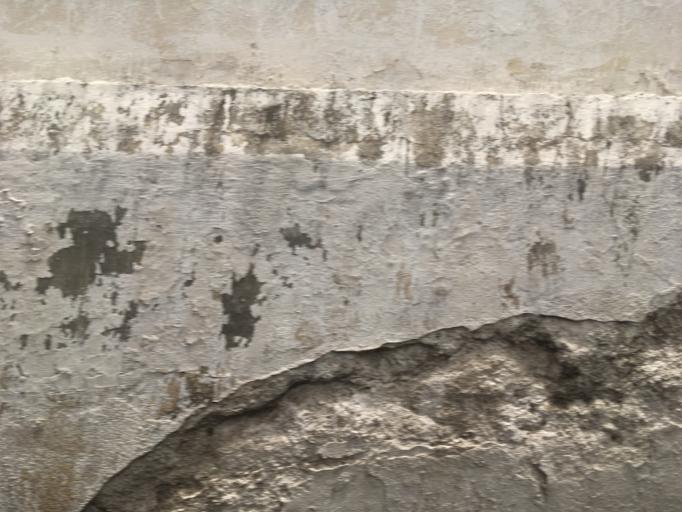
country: BR
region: Rio de Janeiro
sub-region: Rio De Janeiro
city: Rio de Janeiro
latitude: -22.9030
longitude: -43.2438
